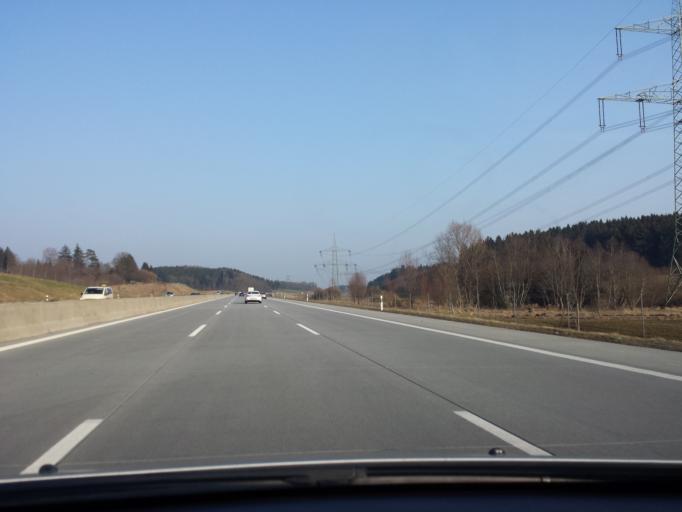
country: DE
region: Bavaria
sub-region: Swabia
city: Dasing
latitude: 48.4002
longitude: 11.0060
